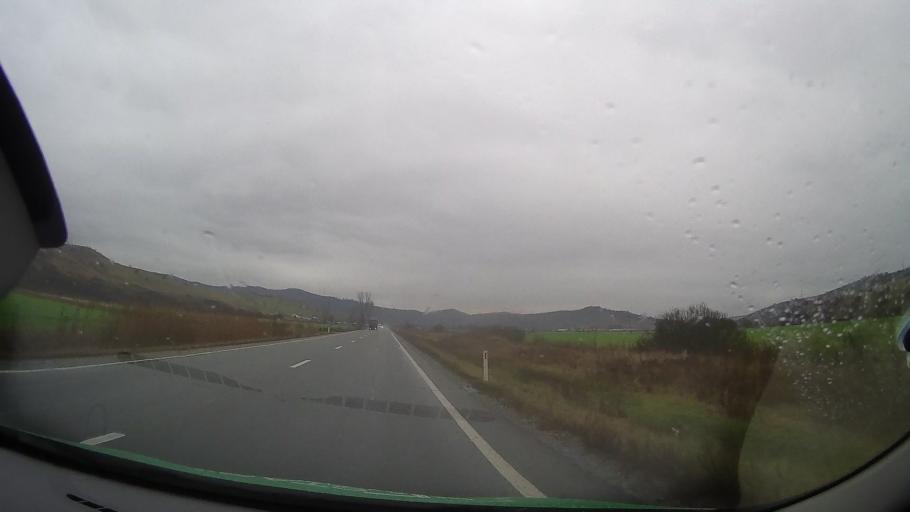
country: RO
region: Bistrita-Nasaud
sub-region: Comuna Teaca
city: Teaca
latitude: 46.9256
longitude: 24.4866
